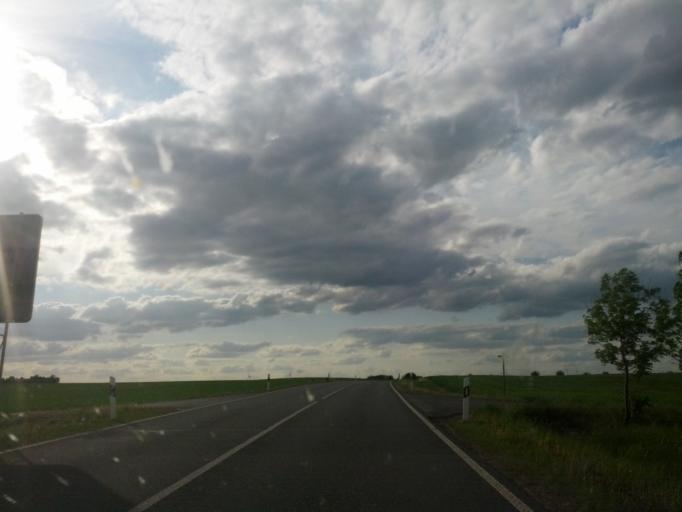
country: DE
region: Thuringia
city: Ernstroda
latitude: 50.8982
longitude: 10.6187
